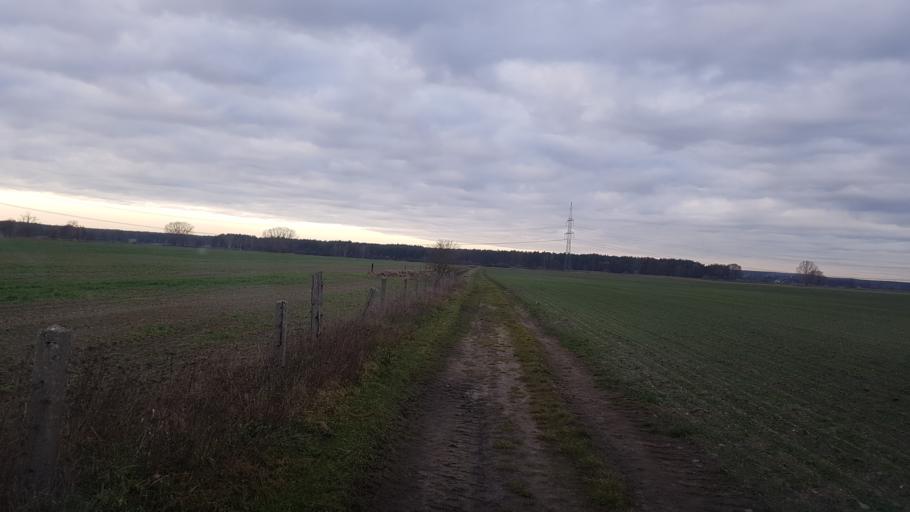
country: DE
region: Brandenburg
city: Schonborn
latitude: 51.5723
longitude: 13.5201
